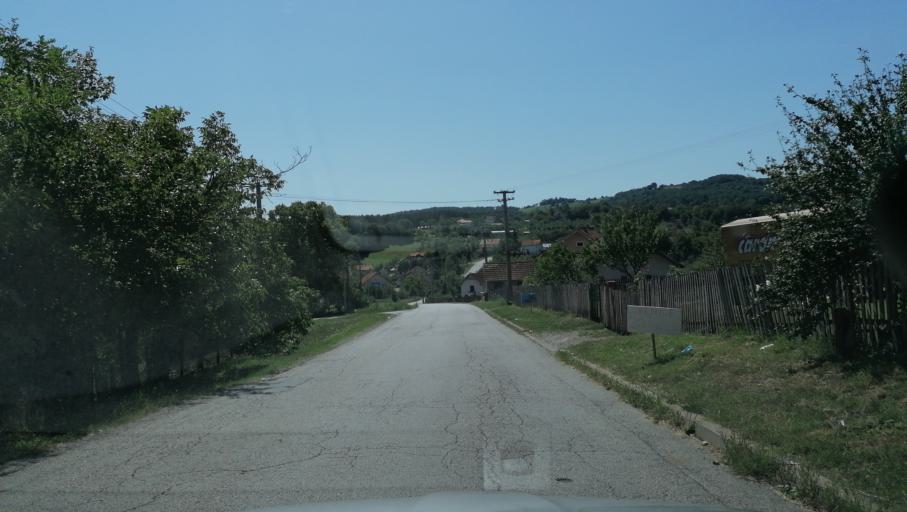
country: RS
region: Central Serbia
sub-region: Kolubarski Okrug
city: Valjevo
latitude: 44.2584
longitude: 19.8774
